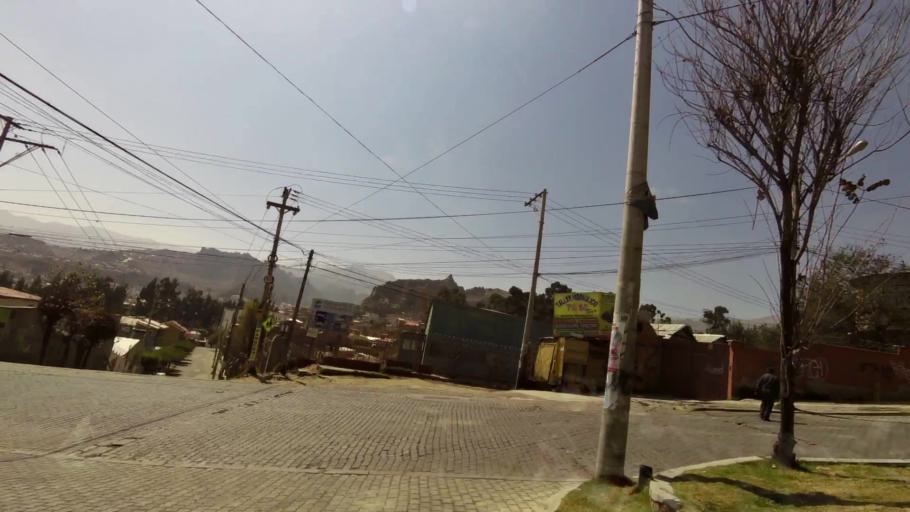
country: BO
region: La Paz
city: La Paz
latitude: -16.5398
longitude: -68.0711
